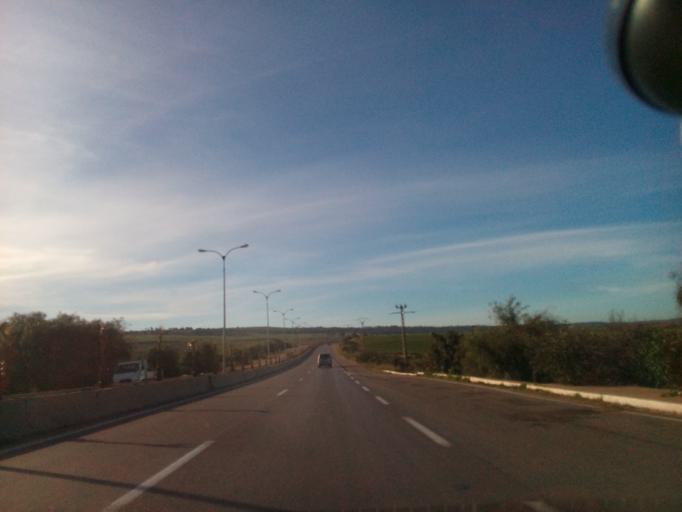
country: DZ
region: Mostaganem
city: Mostaganem
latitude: 35.8296
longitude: -0.0110
